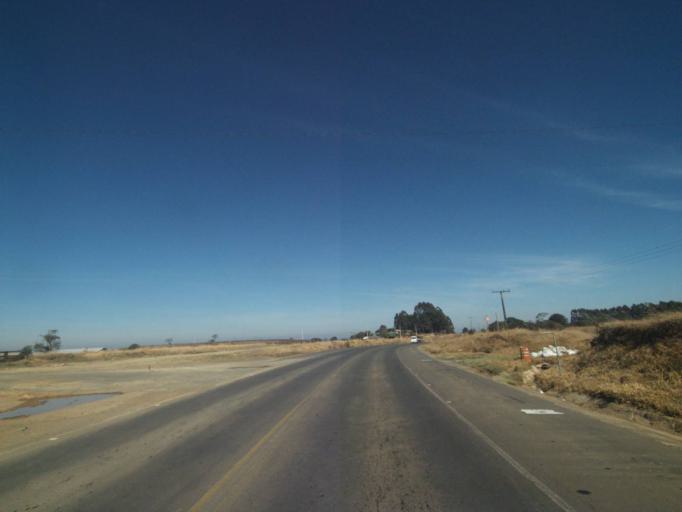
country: BR
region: Parana
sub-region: Tibagi
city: Tibagi
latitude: -24.8004
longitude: -50.4677
